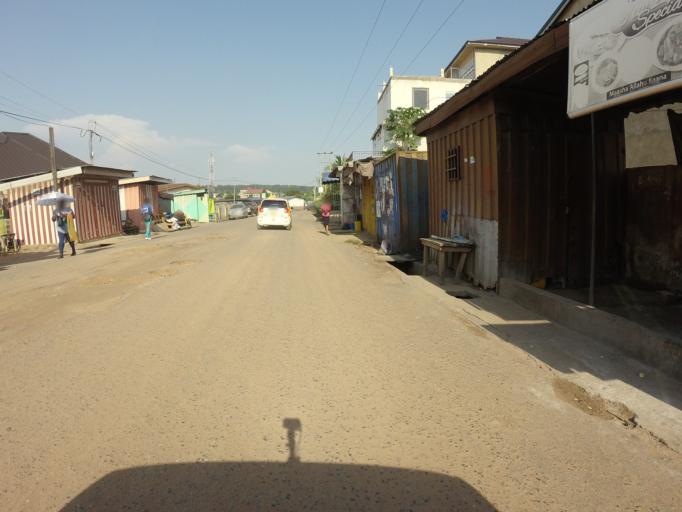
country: GH
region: Greater Accra
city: Dome
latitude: 5.6134
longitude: -0.2370
